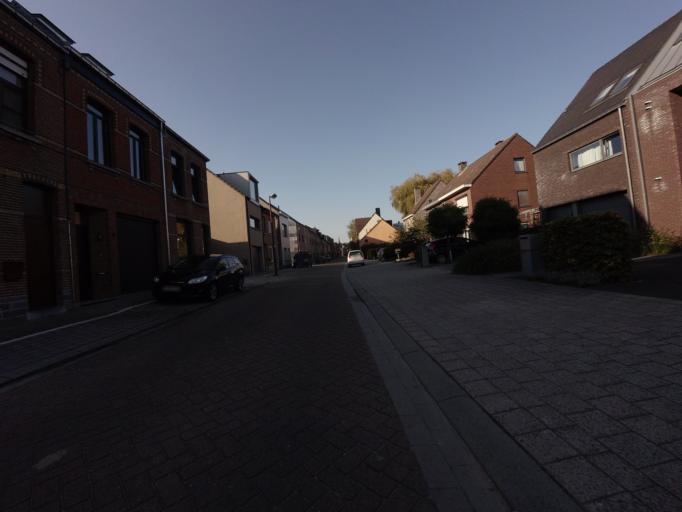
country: BE
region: Flanders
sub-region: Provincie Antwerpen
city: Lint
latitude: 51.1242
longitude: 4.4980
